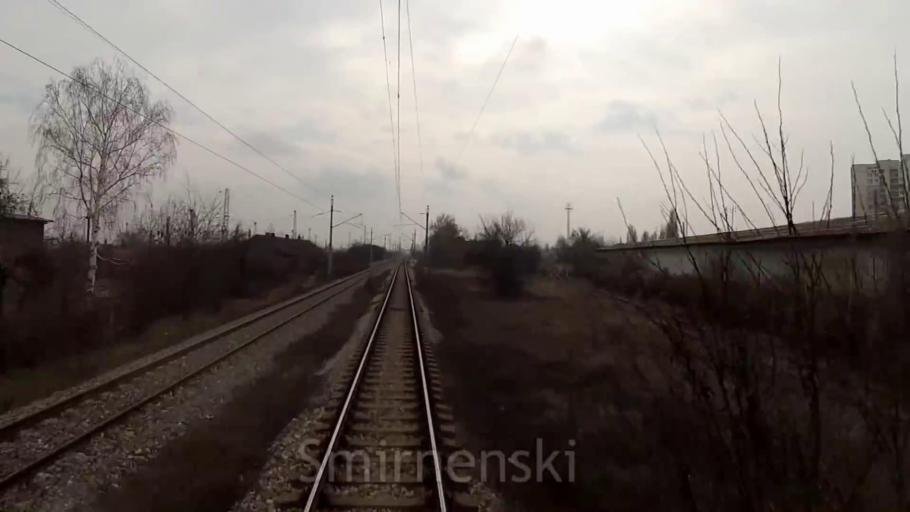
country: BG
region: Sofia-Capital
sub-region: Stolichna Obshtina
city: Sofia
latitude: 42.6705
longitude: 23.4018
